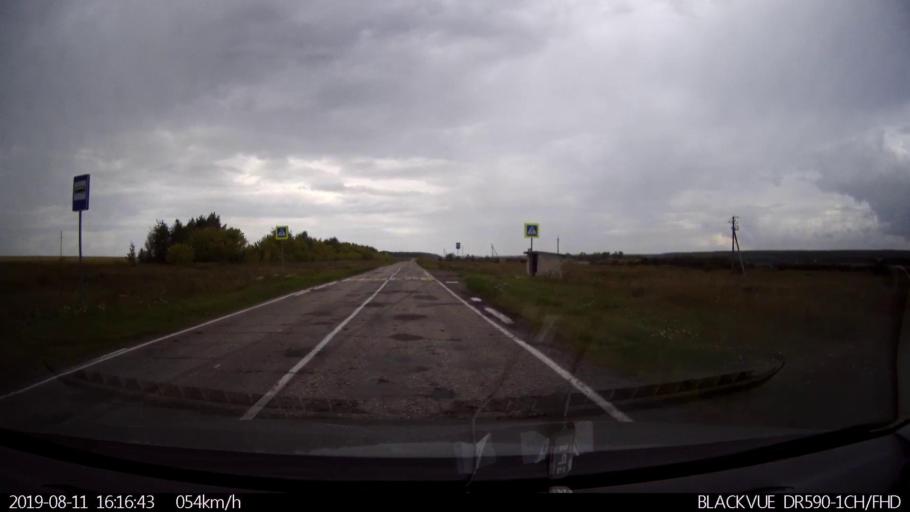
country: RU
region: Ulyanovsk
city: Mayna
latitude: 54.0432
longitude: 47.6199
